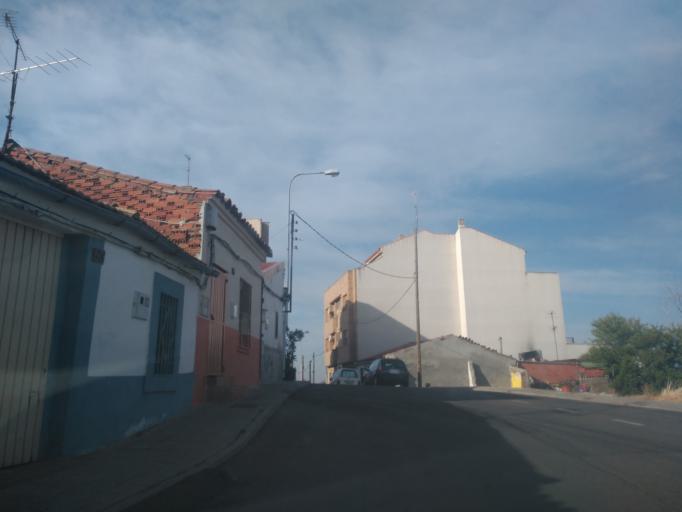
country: ES
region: Castille and Leon
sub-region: Provincia de Salamanca
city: Salamanca
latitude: 40.9793
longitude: -5.6788
